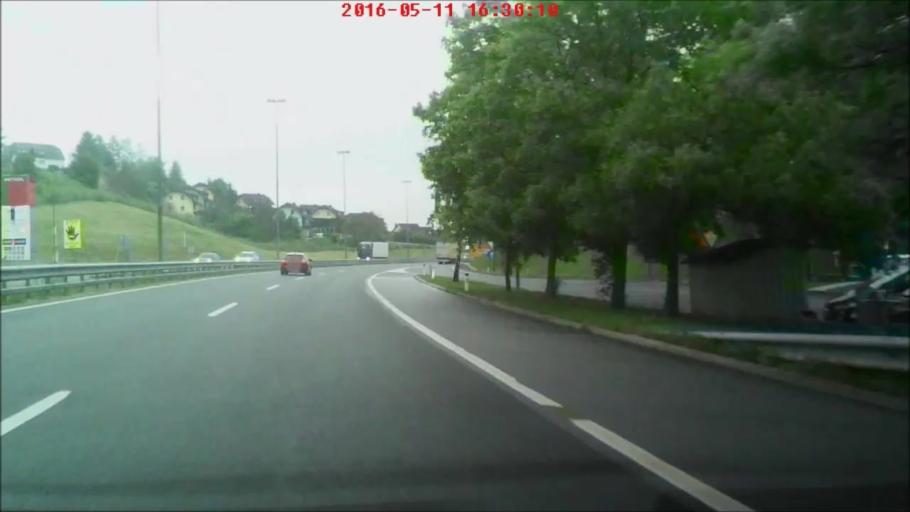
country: SI
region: Sentilj
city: Sentilj v Slov. Goricah
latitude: 46.6864
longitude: 15.6492
